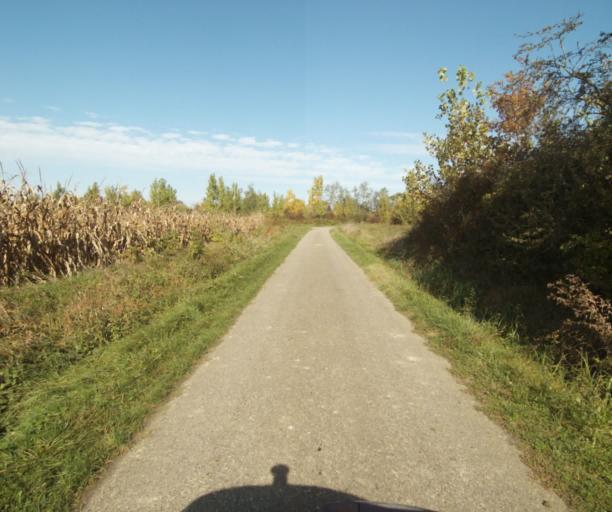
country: FR
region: Midi-Pyrenees
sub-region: Departement du Tarn-et-Garonne
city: Finhan
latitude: 43.9110
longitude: 1.2145
